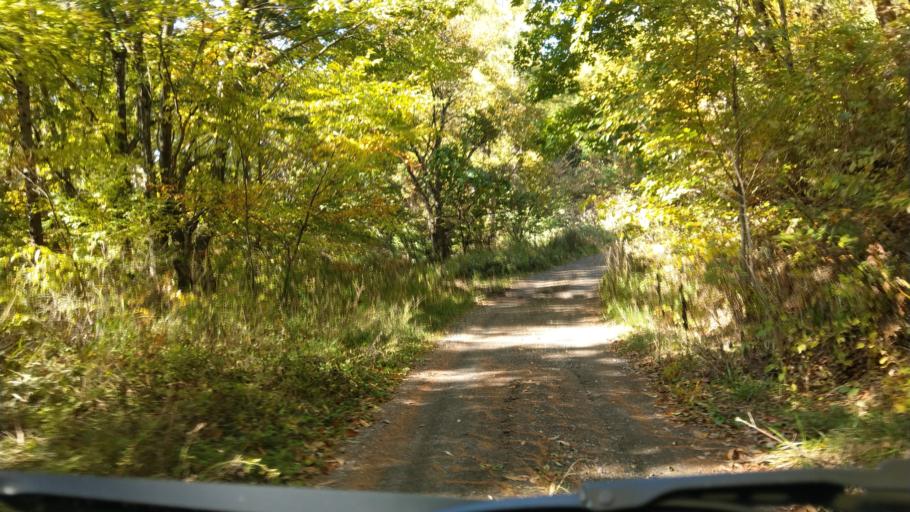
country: JP
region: Nagano
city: Komoro
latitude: 36.3728
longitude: 138.4386
